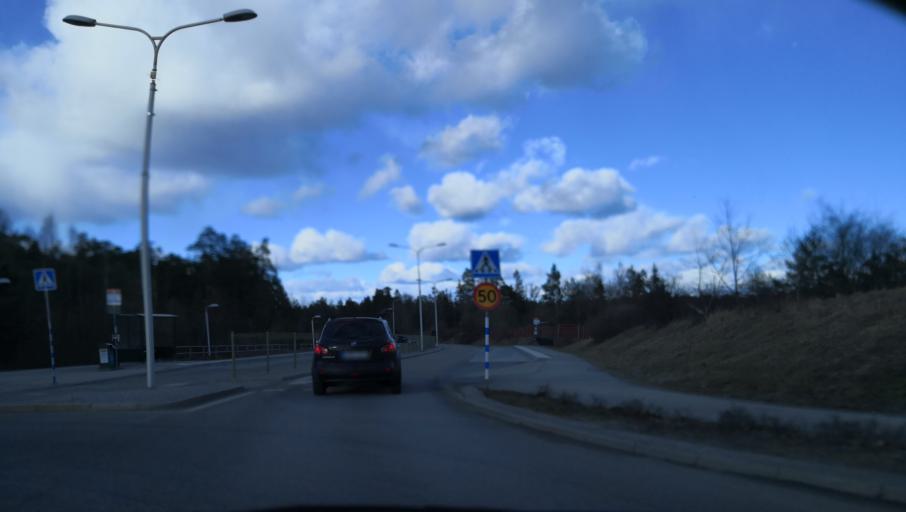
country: SE
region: Stockholm
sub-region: Varmdo Kommun
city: Gustavsberg
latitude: 59.3127
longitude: 18.3895
